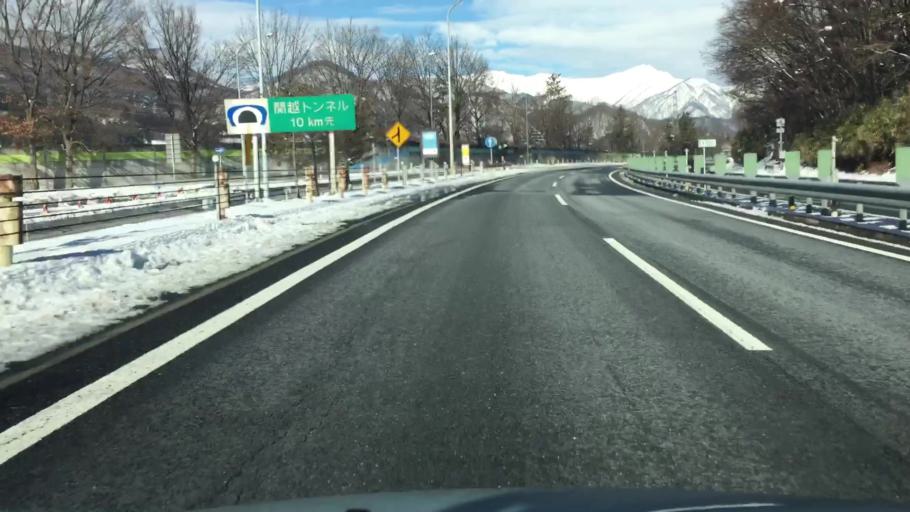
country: JP
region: Gunma
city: Numata
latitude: 36.7020
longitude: 138.9855
